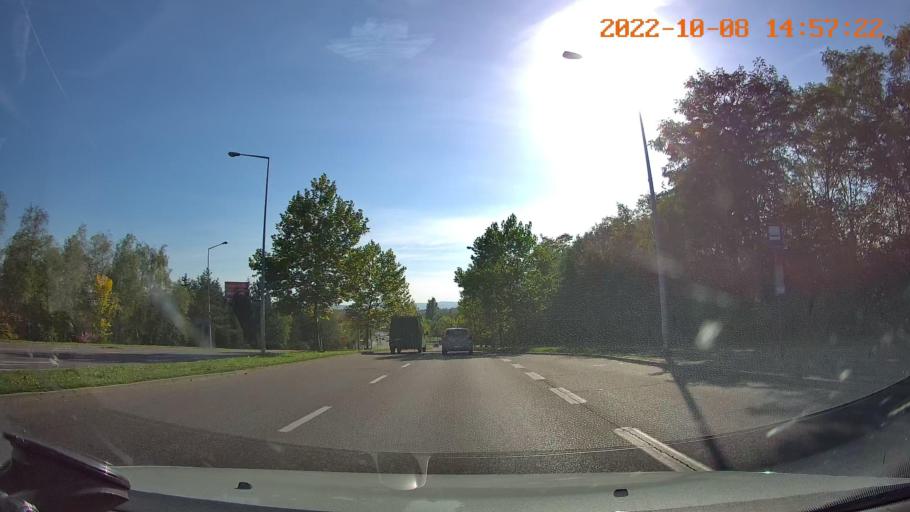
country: PL
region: Lesser Poland Voivodeship
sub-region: Powiat tarnowski
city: Tarnow
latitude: 50.0318
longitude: 20.9997
